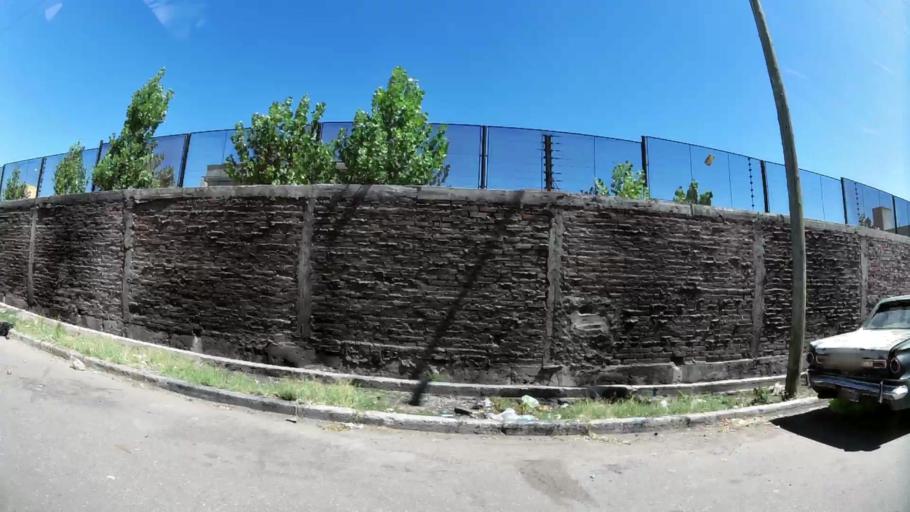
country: AR
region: Mendoza
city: Las Heras
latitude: -32.8516
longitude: -68.8747
